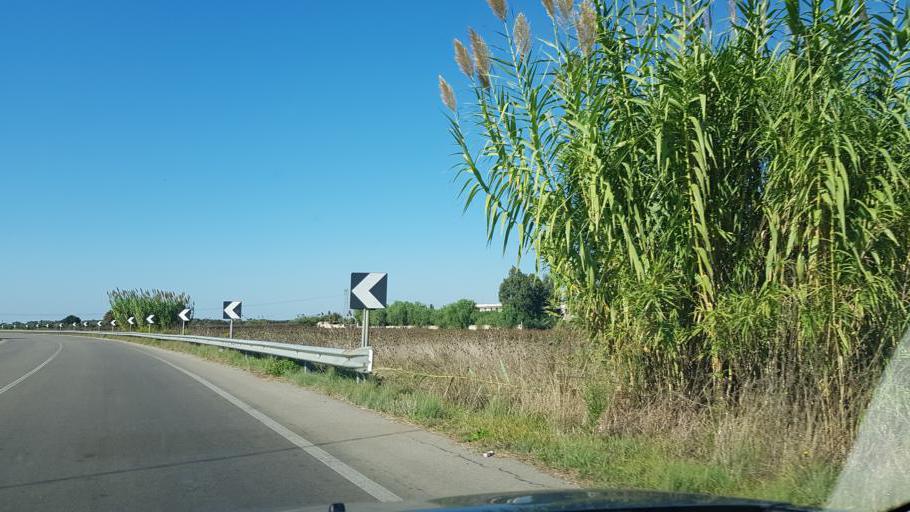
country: IT
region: Apulia
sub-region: Provincia di Lecce
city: Carmiano
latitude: 40.3120
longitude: 18.0256
